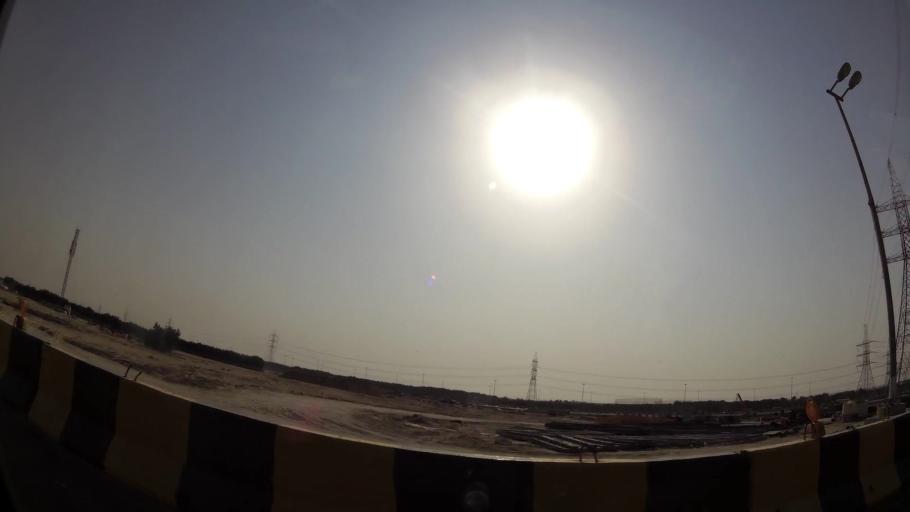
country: KW
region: Muhafazat al Jahra'
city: Al Jahra'
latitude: 29.2963
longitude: 47.7877
